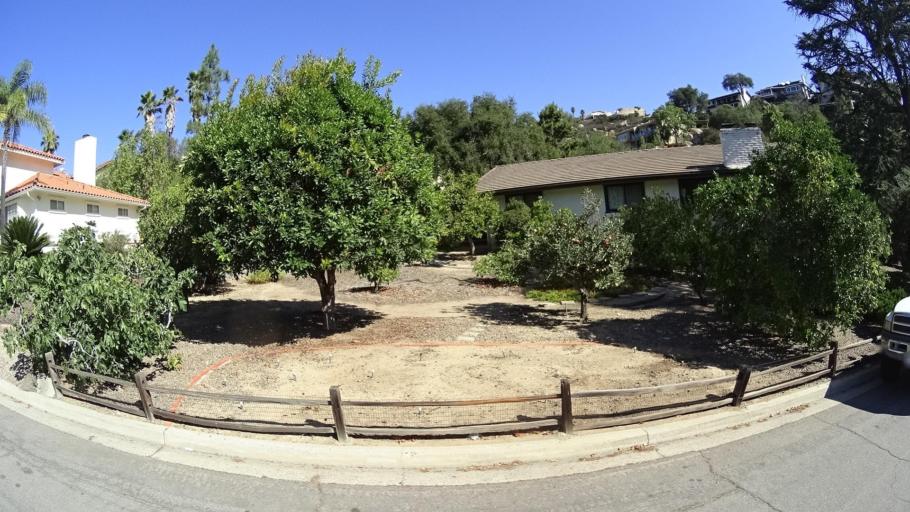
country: US
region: California
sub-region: San Diego County
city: Hidden Meadows
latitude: 33.2172
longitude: -117.1204
